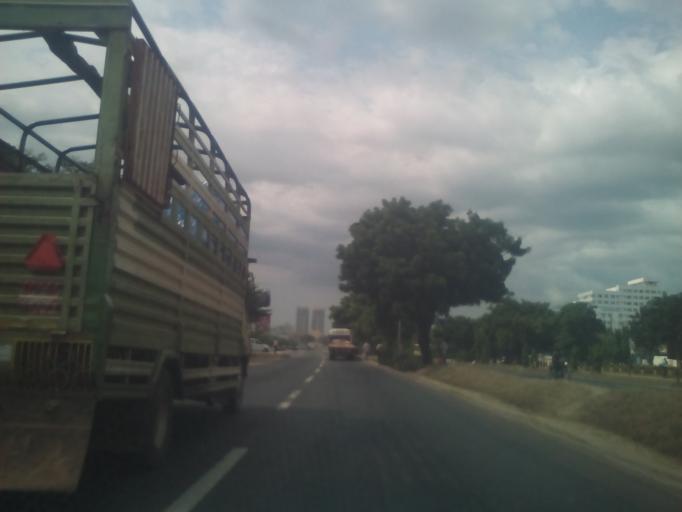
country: TZ
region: Dar es Salaam
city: Dar es Salaam
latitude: -6.8339
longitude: 39.2657
